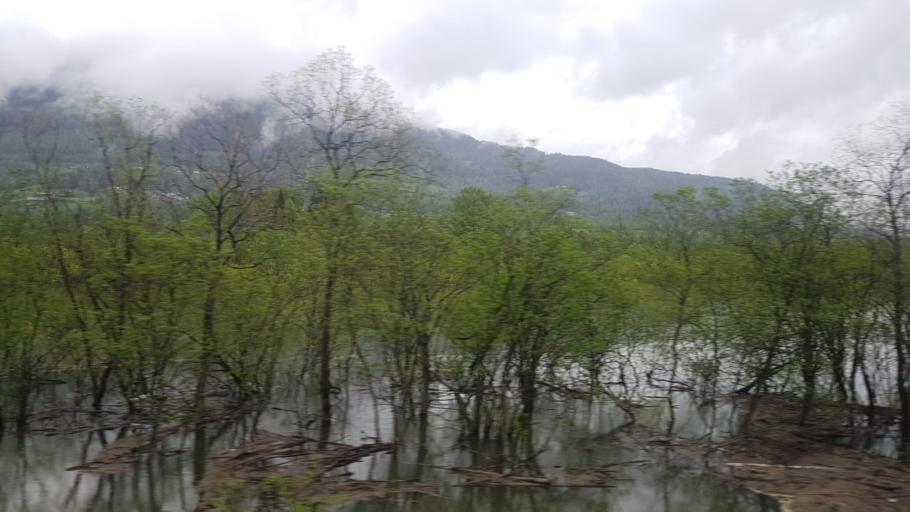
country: NO
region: Oppland
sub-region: Ringebu
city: Ringebu
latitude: 61.4594
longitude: 10.2003
